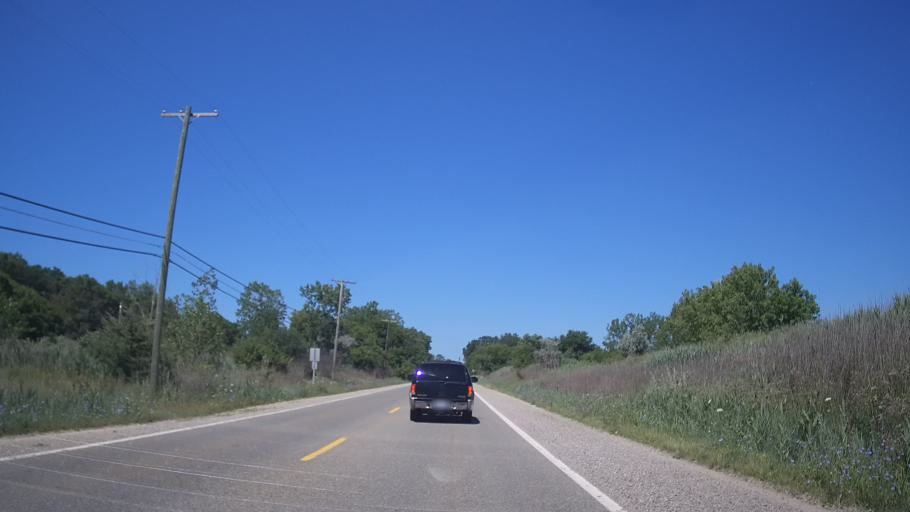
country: US
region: Michigan
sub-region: Macomb County
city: Shelby
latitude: 42.6520
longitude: -83.0804
